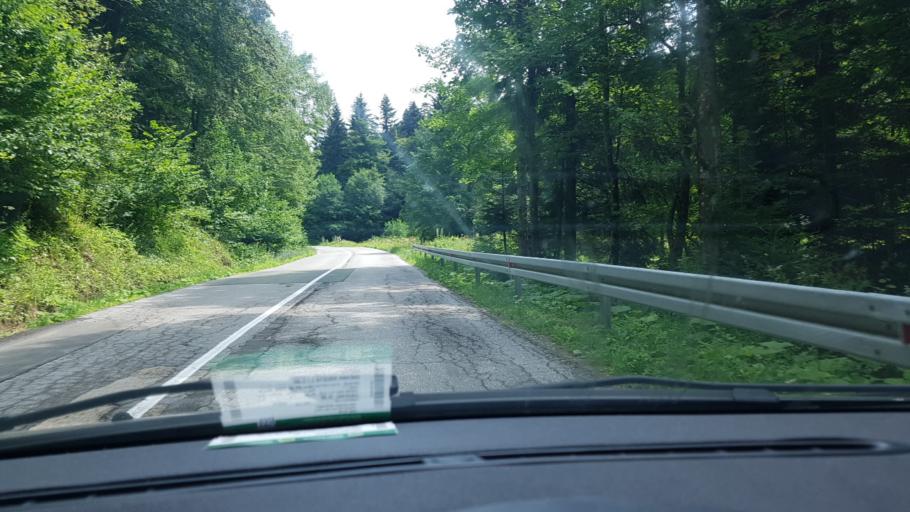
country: HR
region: Primorsko-Goranska
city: Hreljin
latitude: 45.3320
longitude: 14.6804
